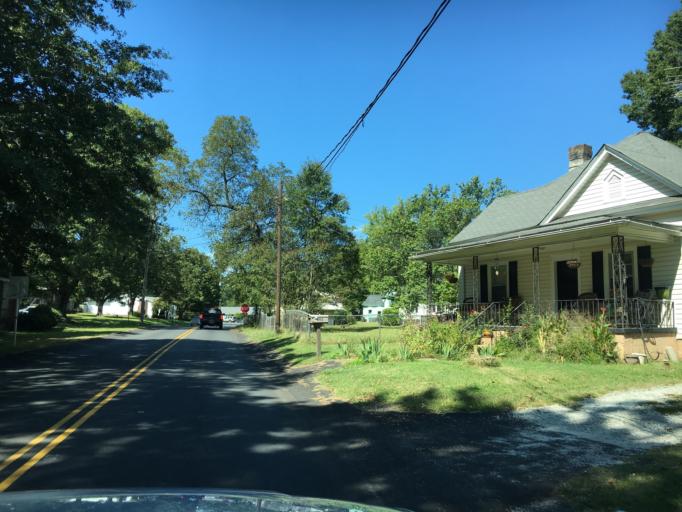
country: US
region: South Carolina
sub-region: Greenville County
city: Greer
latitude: 34.9313
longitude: -82.2241
